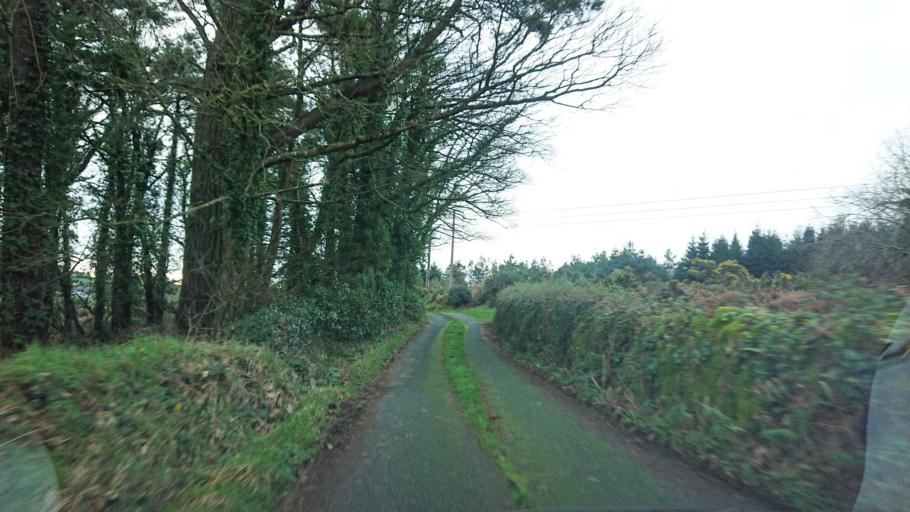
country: IE
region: Leinster
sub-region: Kilkenny
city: Mooncoin
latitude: 52.2153
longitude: -7.2717
